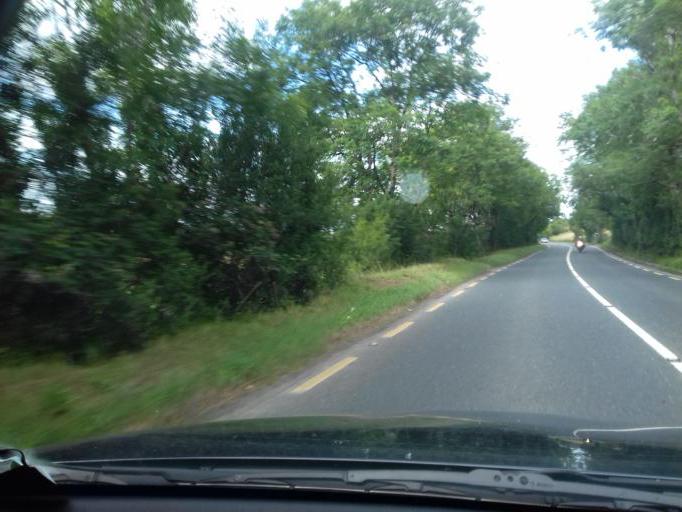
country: IE
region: Leinster
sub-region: Wicklow
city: Valleymount
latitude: 53.0532
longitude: -6.6284
